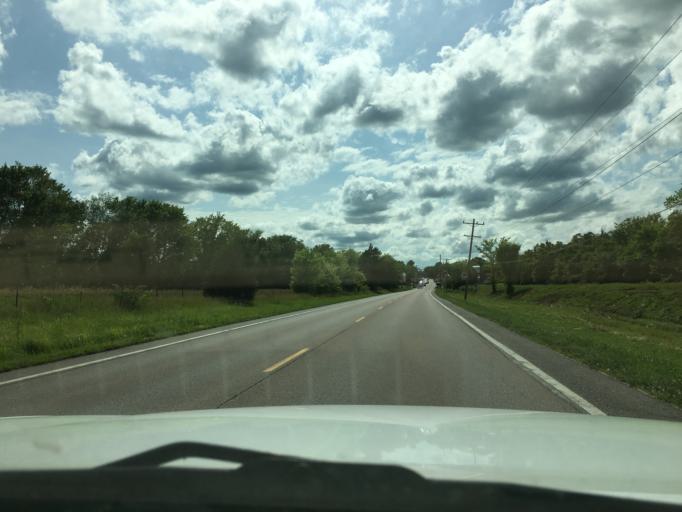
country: US
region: Missouri
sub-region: Franklin County
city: Gerald
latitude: 38.3873
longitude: -91.3943
